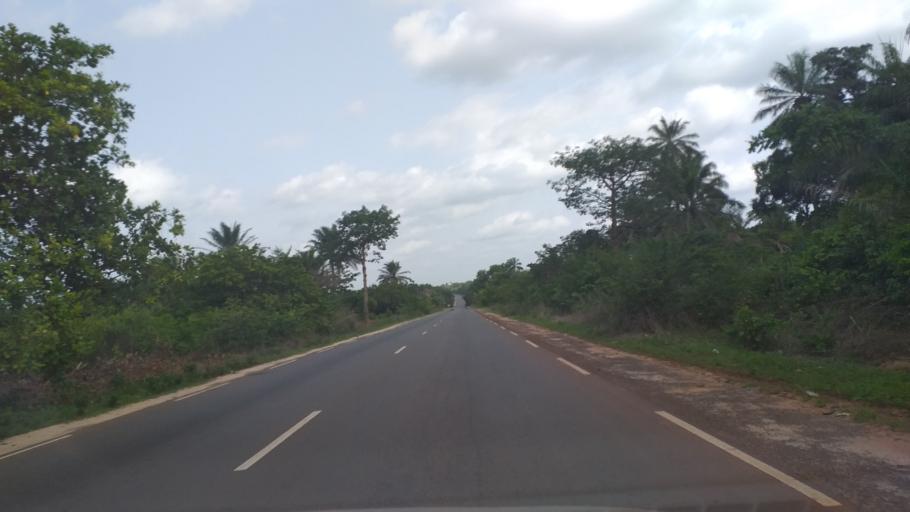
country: GN
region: Boke
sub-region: Boke Prefecture
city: Sangueya
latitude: 10.7409
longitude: -14.3792
